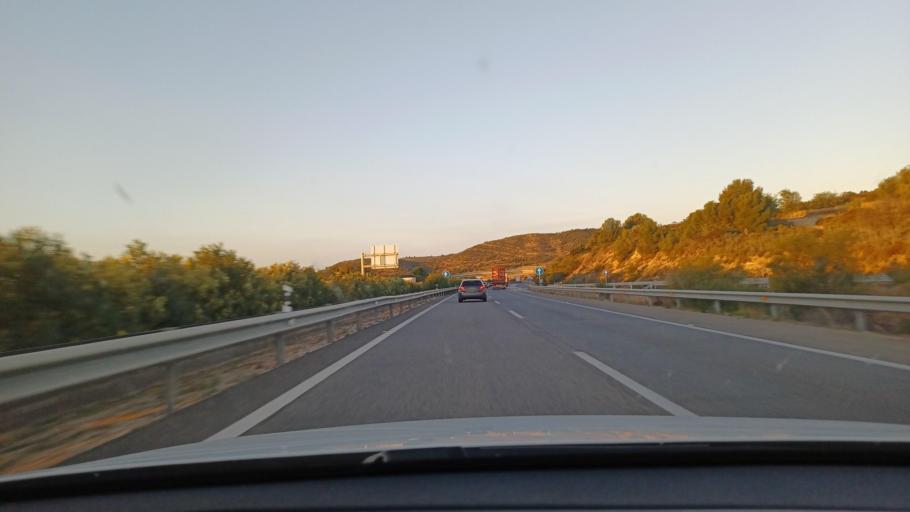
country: ES
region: Valencia
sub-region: Provincia de Castello
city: Torreblanca
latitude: 40.2277
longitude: 0.2021
